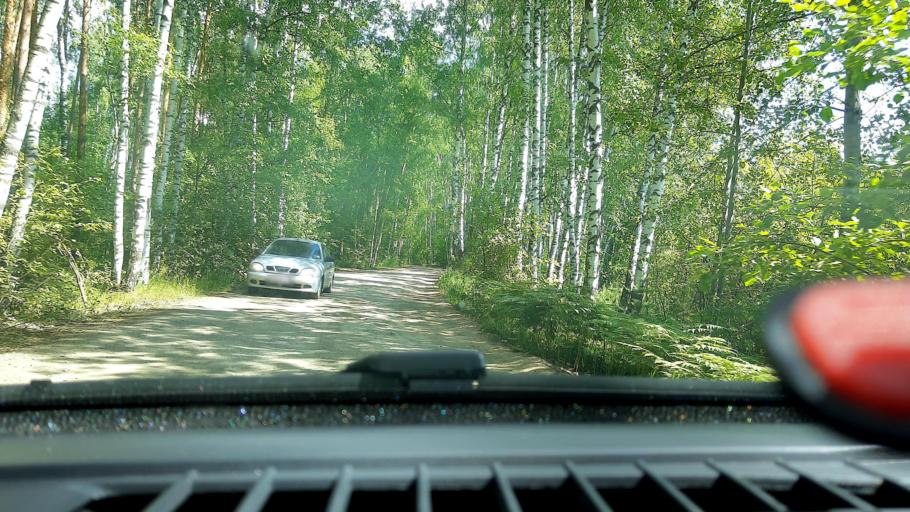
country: RU
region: Nizjnij Novgorod
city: Gorbatovka
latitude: 56.2962
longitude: 43.8178
